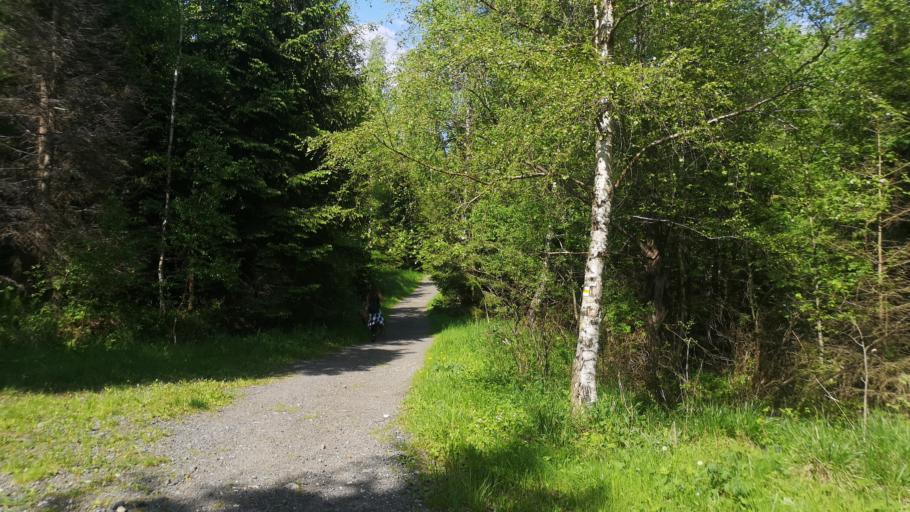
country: SK
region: Presovsky
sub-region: Okres Poprad
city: Nova Lesna
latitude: 49.1738
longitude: 20.2847
